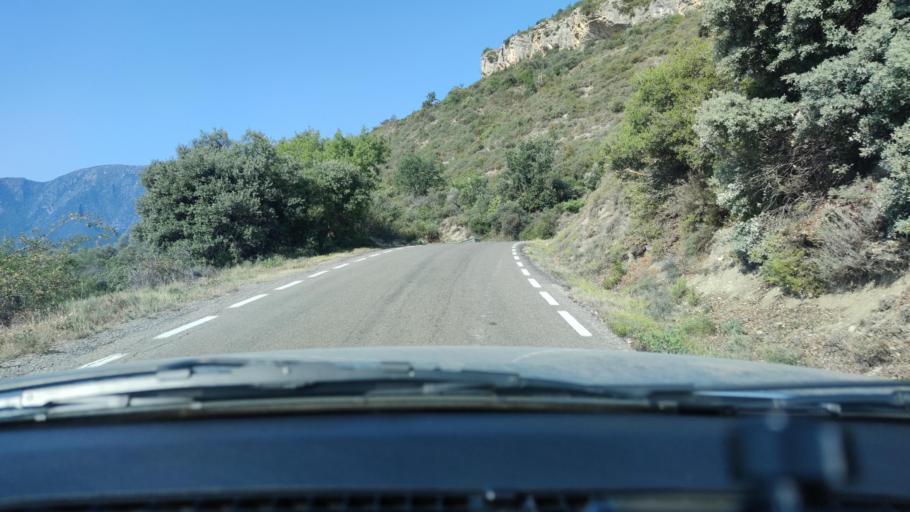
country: ES
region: Catalonia
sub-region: Provincia de Lleida
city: Llimiana
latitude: 42.0861
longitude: 0.8660
